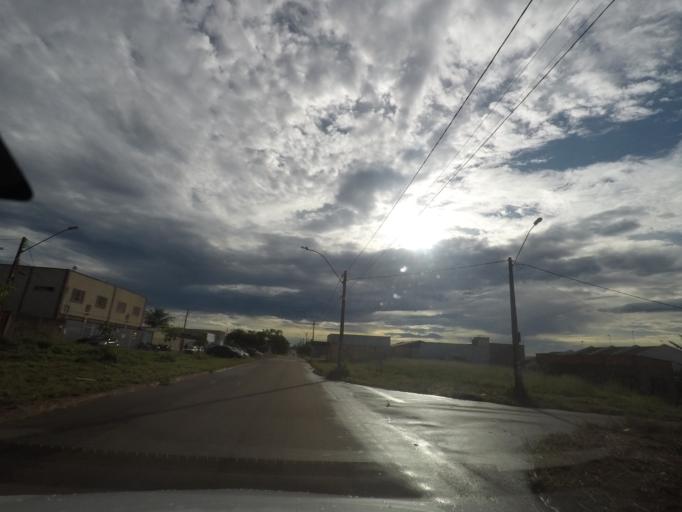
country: BR
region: Goias
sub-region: Aparecida De Goiania
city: Aparecida de Goiania
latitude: -16.7626
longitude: -49.3625
